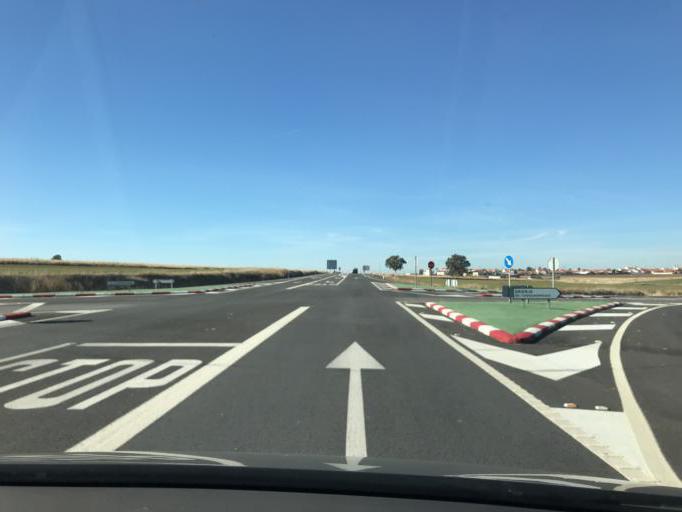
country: ES
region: Extremadura
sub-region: Provincia de Badajoz
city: Granja de Torrehermosa
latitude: 38.3004
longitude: -5.5837
